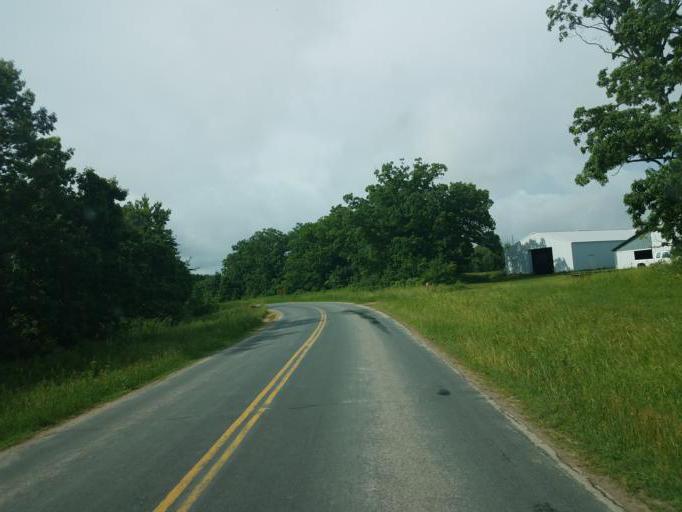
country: US
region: Wisconsin
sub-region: Juneau County
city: Elroy
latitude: 43.8121
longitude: -90.4312
